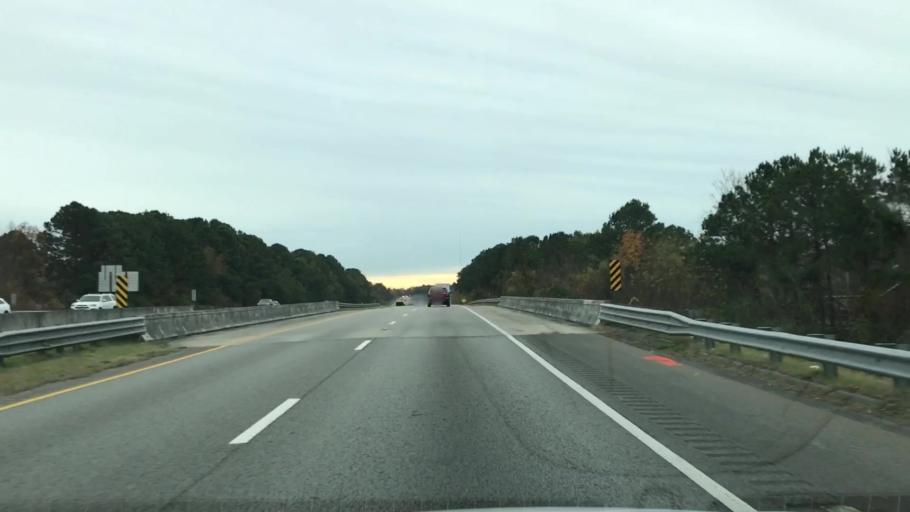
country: US
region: South Carolina
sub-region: Charleston County
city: Mount Pleasant
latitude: 32.8309
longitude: -79.8525
